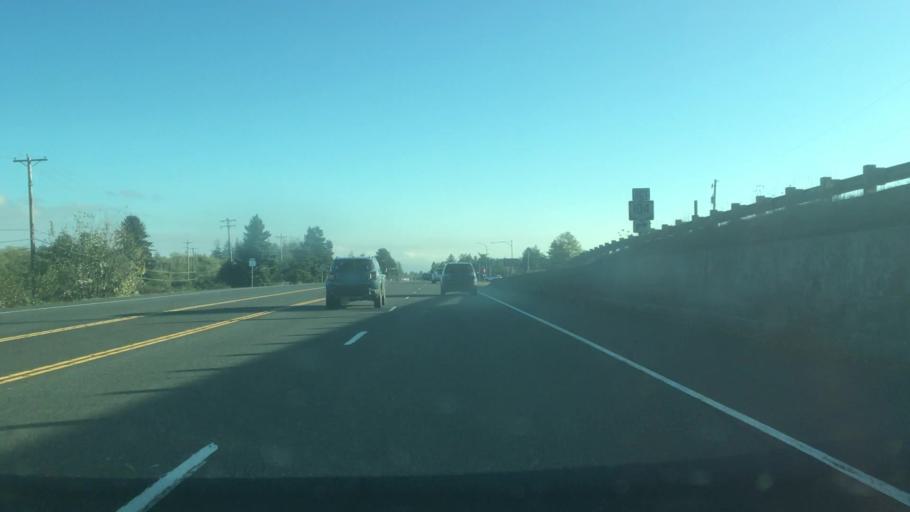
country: US
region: Oregon
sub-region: Clatsop County
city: Warrenton
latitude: 46.1304
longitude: -123.9289
